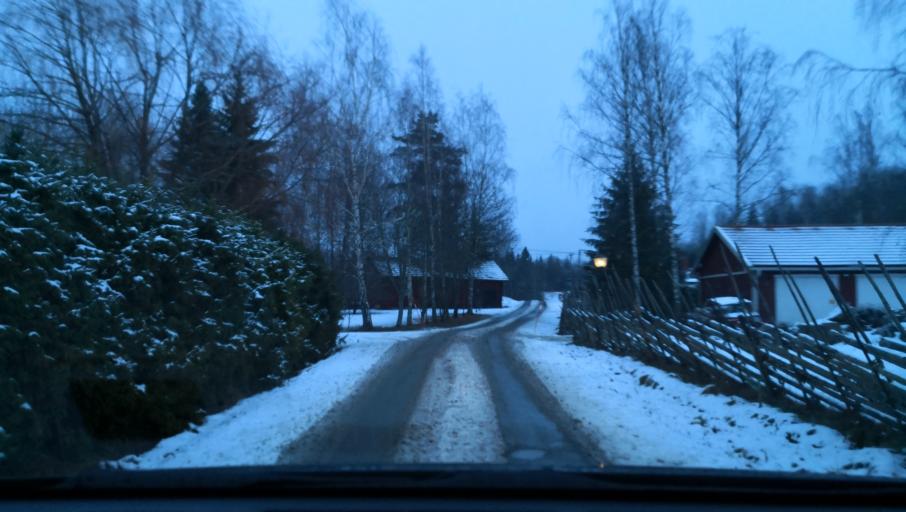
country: SE
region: Soedermanland
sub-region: Eskilstuna Kommun
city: Kvicksund
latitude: 59.3940
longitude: 16.2242
